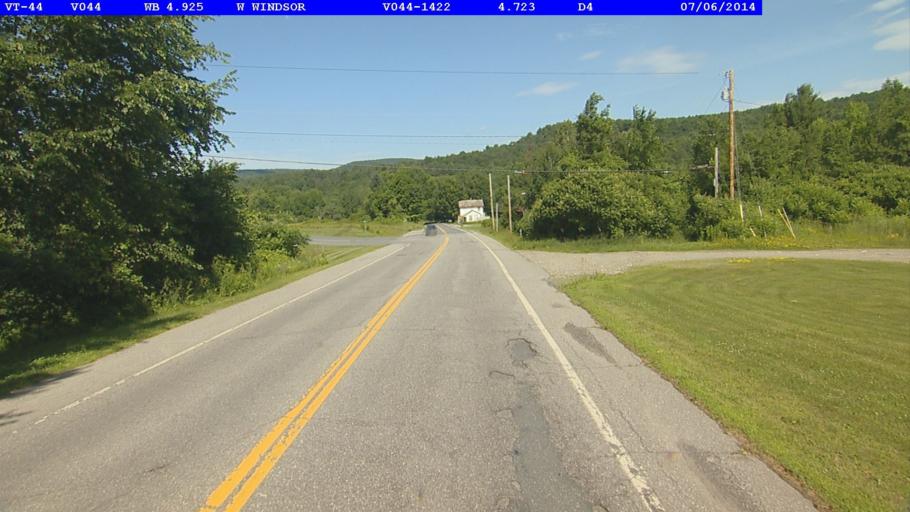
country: US
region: Vermont
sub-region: Windsor County
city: Windsor
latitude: 43.4680
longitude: -72.4591
